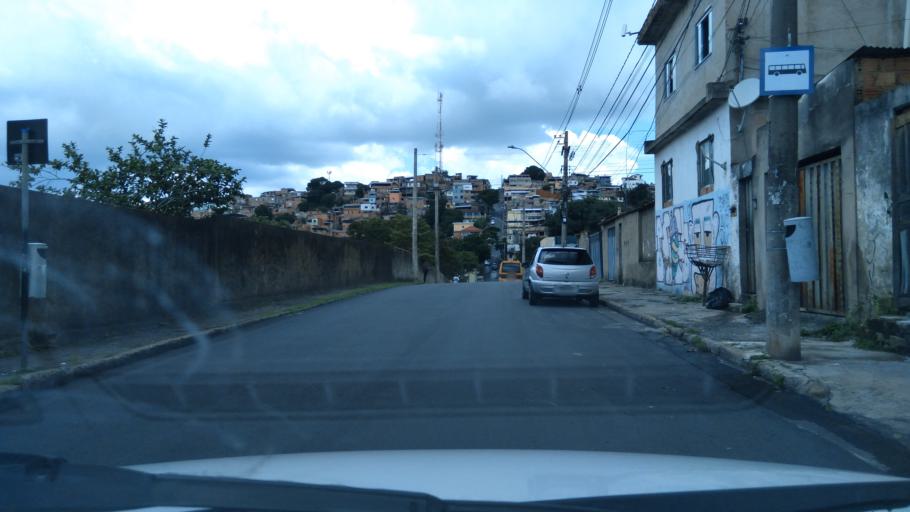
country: BR
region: Minas Gerais
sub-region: Belo Horizonte
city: Belo Horizonte
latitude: -19.9145
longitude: -43.8946
